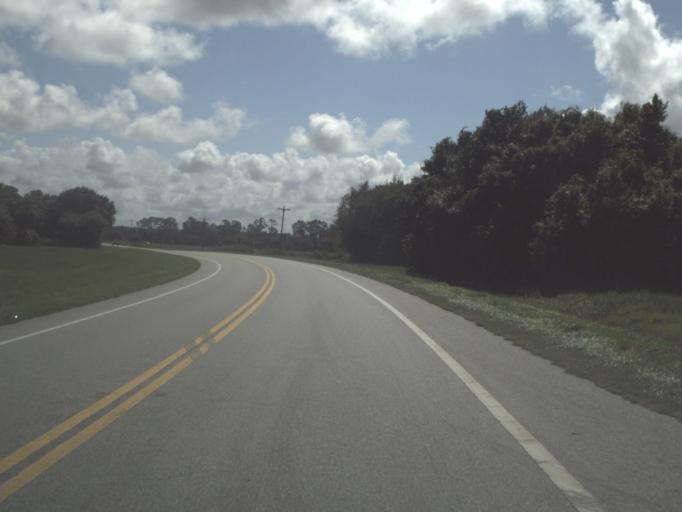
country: US
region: Florida
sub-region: DeSoto County
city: Arcadia
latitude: 27.3283
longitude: -82.1326
